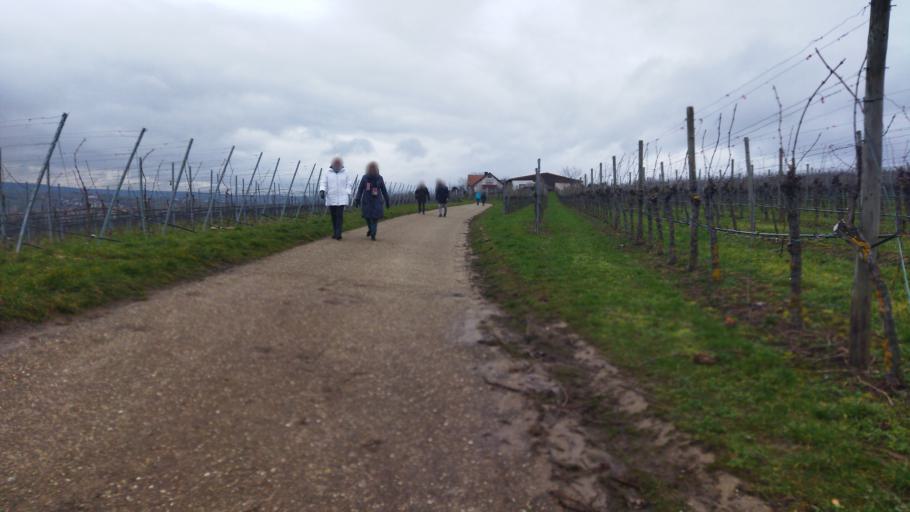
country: DE
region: Baden-Wuerttemberg
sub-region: Regierungsbezirk Stuttgart
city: Talheim
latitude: 49.0690
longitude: 9.1782
